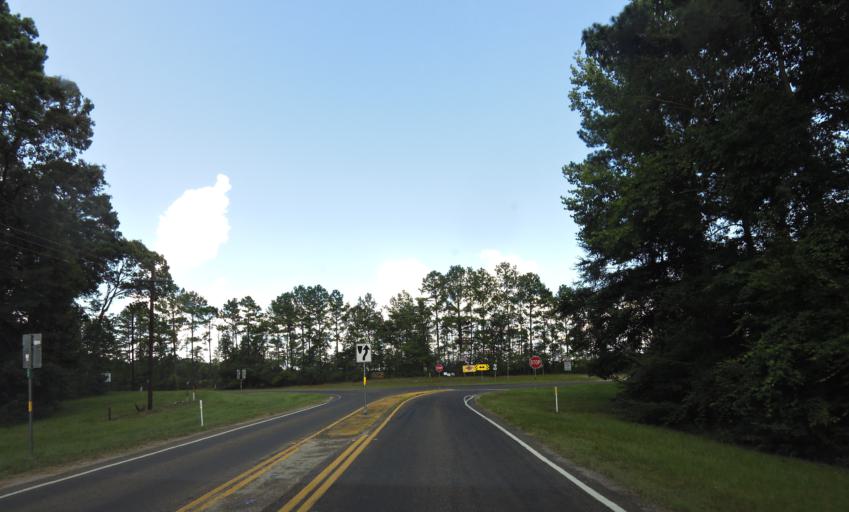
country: US
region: Louisiana
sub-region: Vernon Parish
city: New Llano
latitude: 31.1611
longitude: -93.5730
